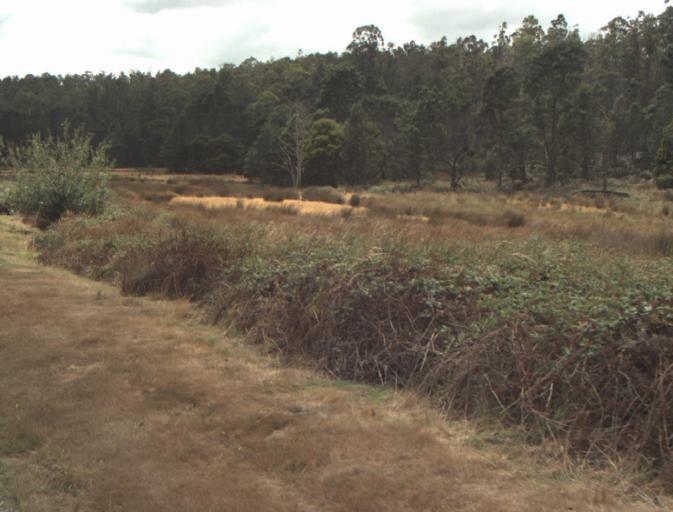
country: AU
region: Tasmania
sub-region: Dorset
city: Bridport
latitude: -41.1887
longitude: 147.2617
